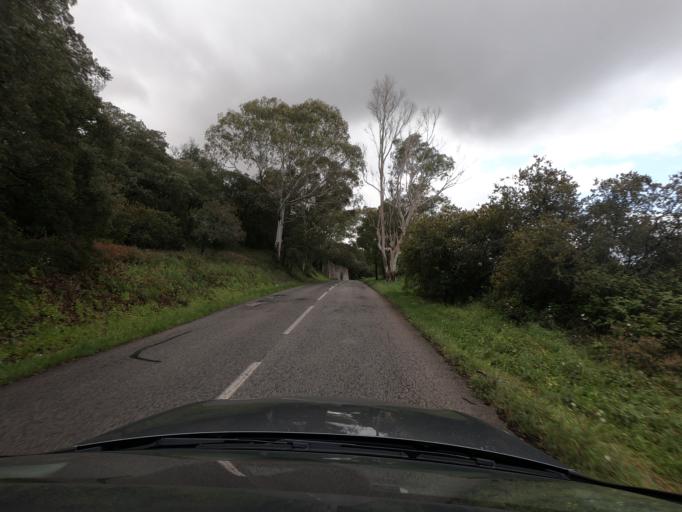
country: PT
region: Lisbon
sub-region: Sintra
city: Queluz
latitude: 38.7433
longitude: -9.2628
